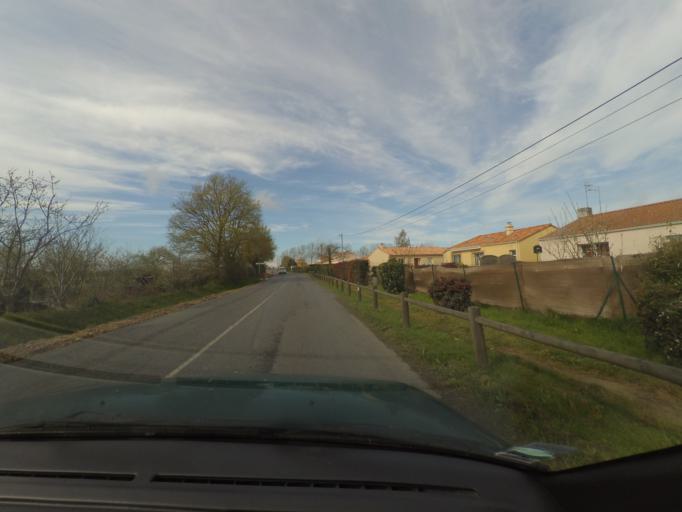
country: FR
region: Pays de la Loire
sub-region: Departement de la Loire-Atlantique
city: Aigrefeuille-sur-Maine
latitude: 47.0743
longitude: -1.4206
